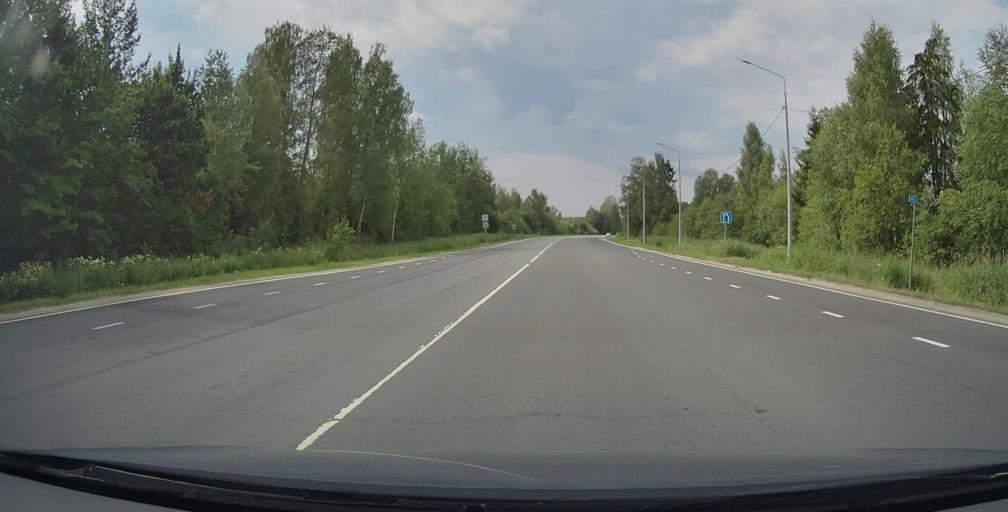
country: RU
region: Jaroslavl
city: Tutayev
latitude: 57.8842
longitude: 39.4459
